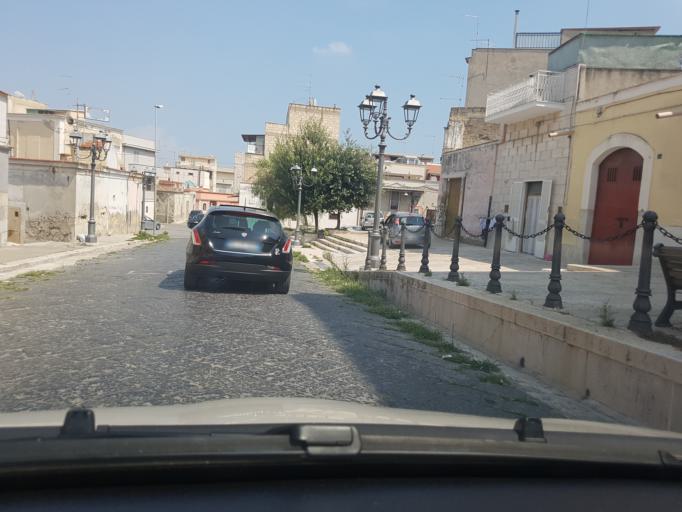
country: IT
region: Apulia
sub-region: Provincia di Foggia
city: Cerignola
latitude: 41.2673
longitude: 15.8926
